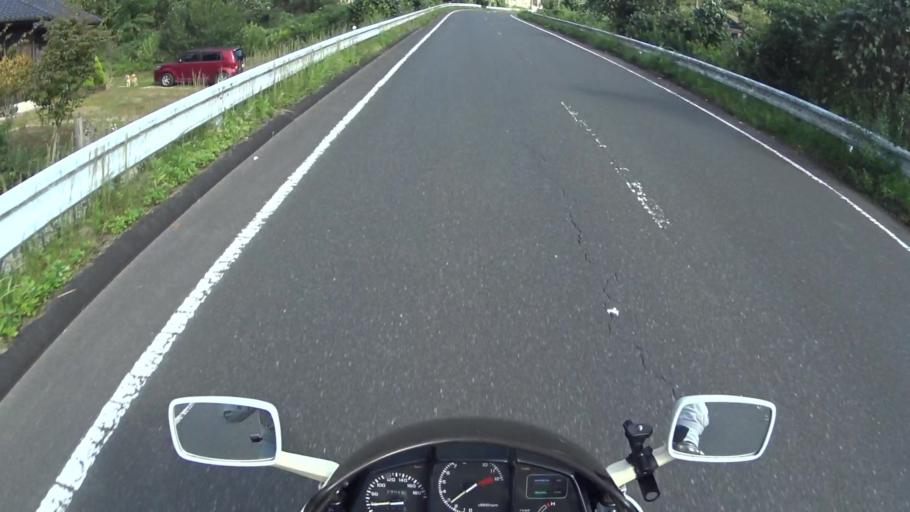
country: JP
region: Kyoto
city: Miyazu
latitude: 35.5750
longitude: 135.1048
